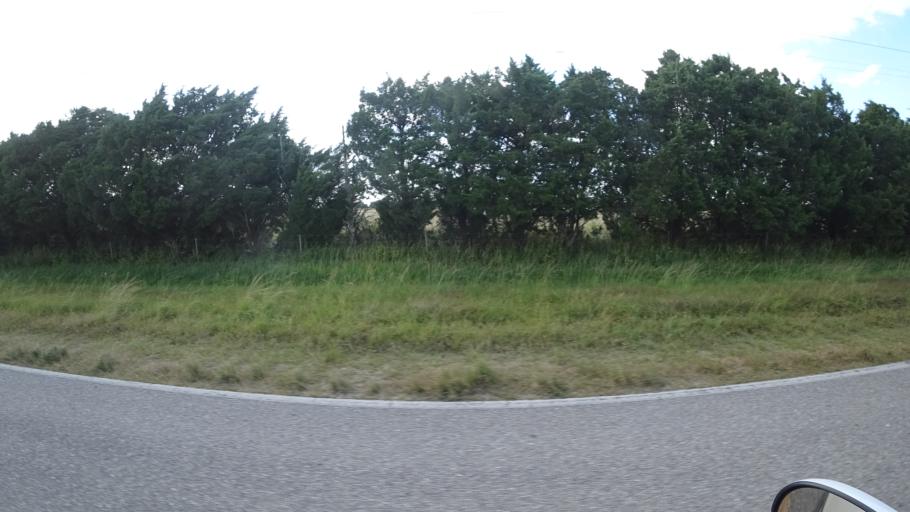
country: US
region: Florida
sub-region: DeSoto County
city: Arcadia
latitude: 27.2961
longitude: -82.1134
